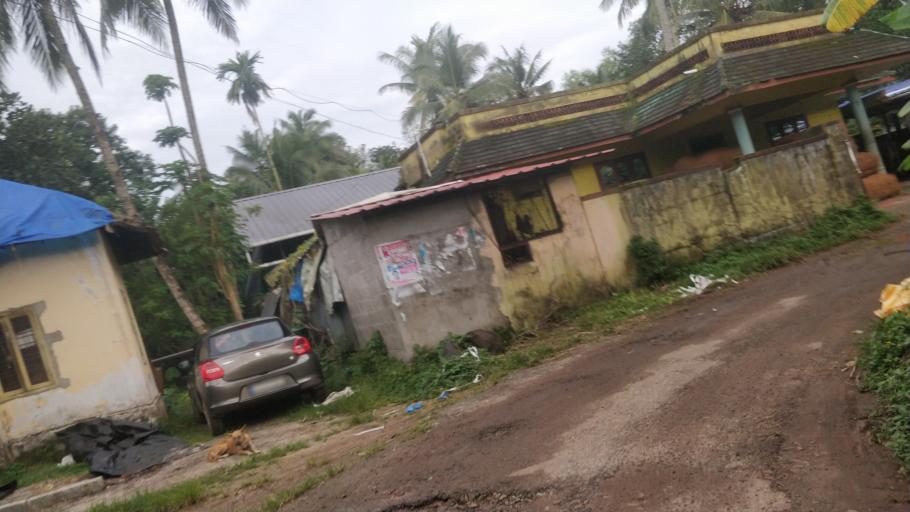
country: IN
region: Kerala
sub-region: Alappuzha
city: Shertallai
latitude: 9.6977
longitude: 76.3598
